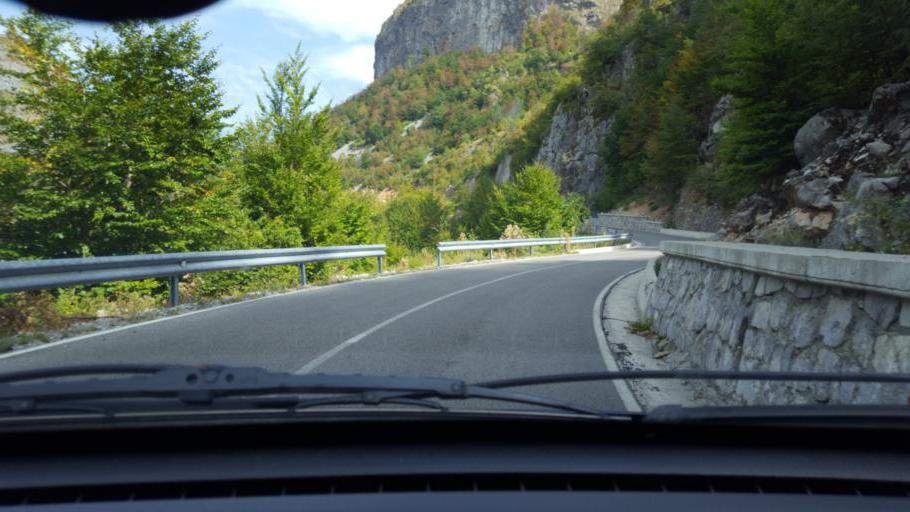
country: ME
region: Andrijevica
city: Andrijevica
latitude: 42.5330
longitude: 19.6673
